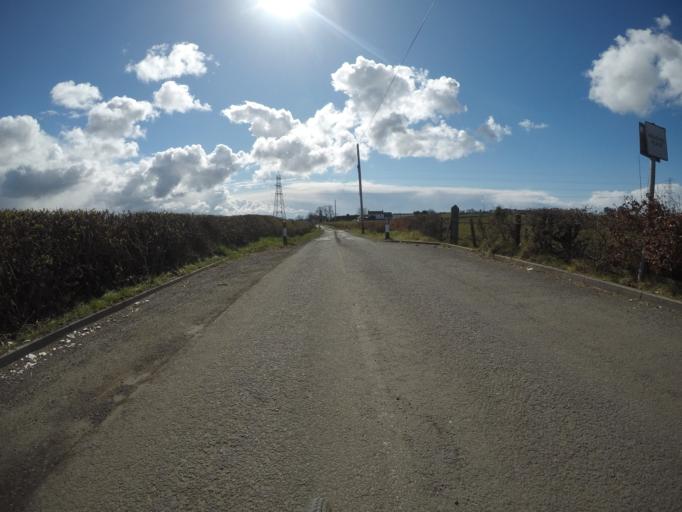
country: GB
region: Scotland
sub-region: North Ayrshire
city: Kilwinning
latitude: 55.6733
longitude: -4.7224
